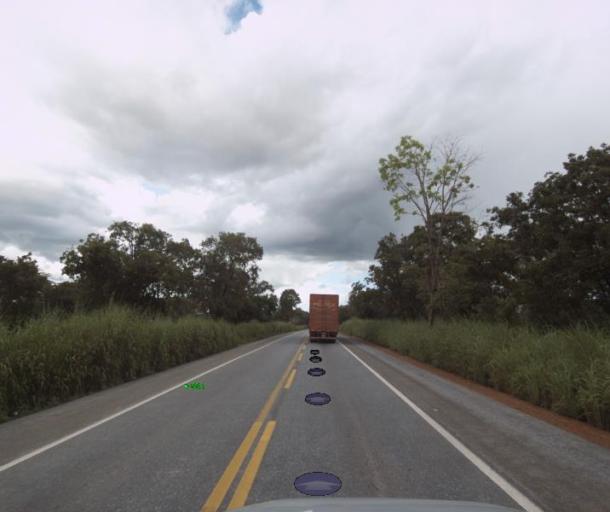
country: BR
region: Goias
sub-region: Porangatu
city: Porangatu
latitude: -13.2977
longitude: -49.1223
